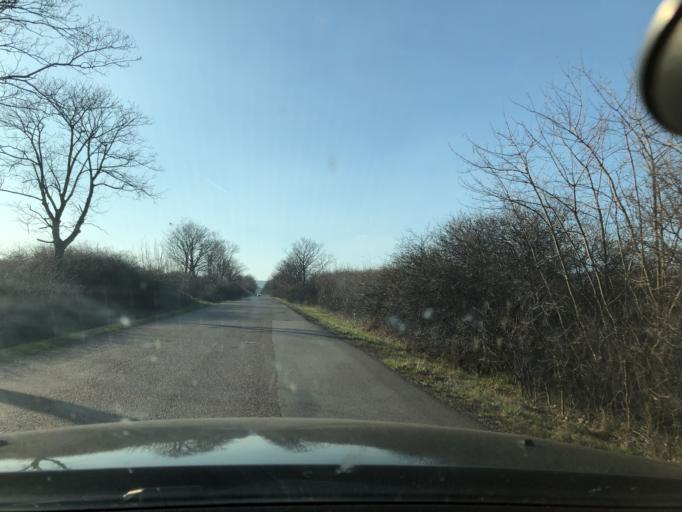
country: HU
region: Nograd
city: Paszto
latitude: 47.9098
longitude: 19.6585
